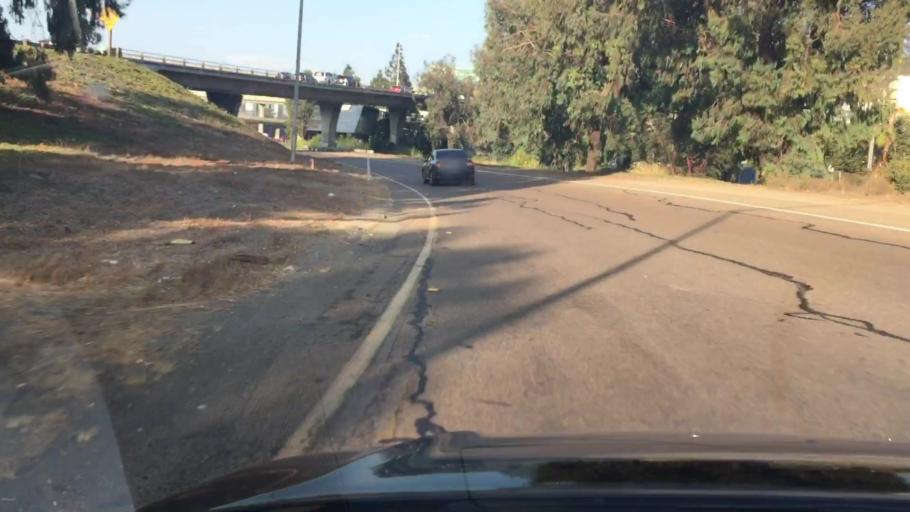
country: US
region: California
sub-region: San Diego County
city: San Diego
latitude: 32.7698
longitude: -117.1364
